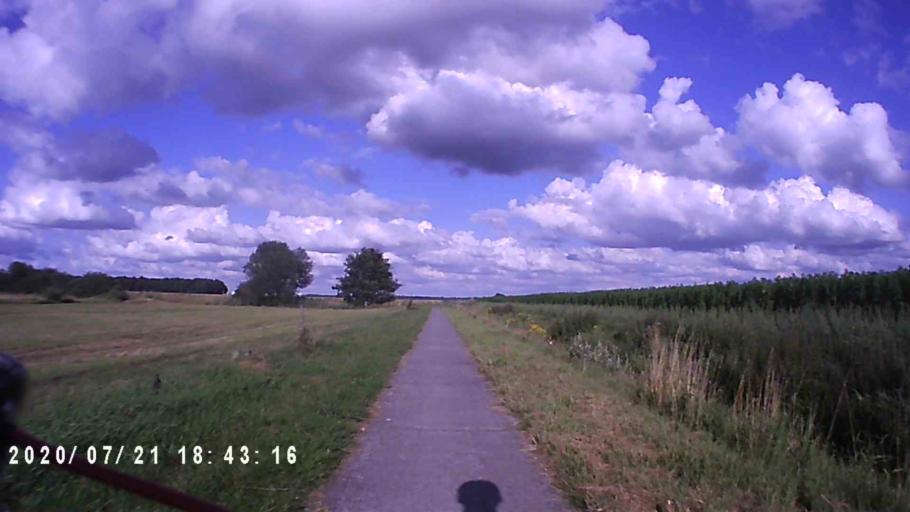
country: NL
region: Groningen
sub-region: Gemeente Hoogezand-Sappemeer
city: Hoogezand
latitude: 53.2027
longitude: 6.7476
